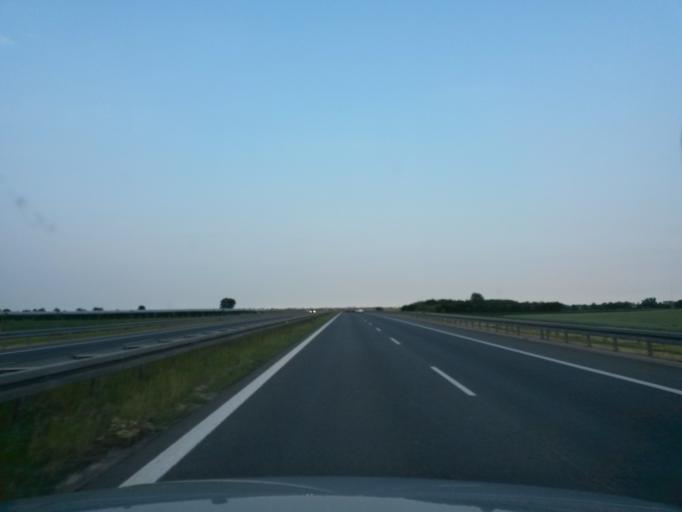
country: PL
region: Lower Silesian Voivodeship
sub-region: Powiat olesnicki
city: Dobroszyce
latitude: 51.2232
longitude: 17.3028
